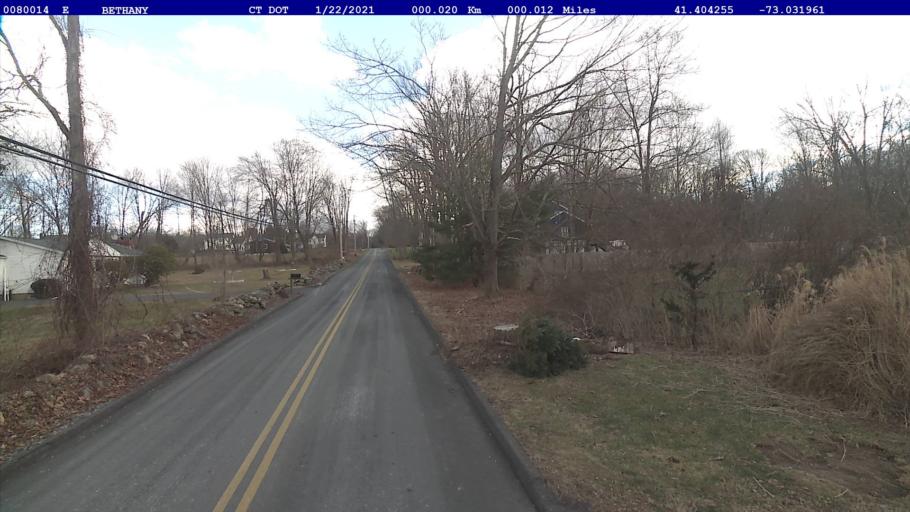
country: US
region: Connecticut
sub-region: New Haven County
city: Seymour
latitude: 41.4042
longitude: -73.0320
